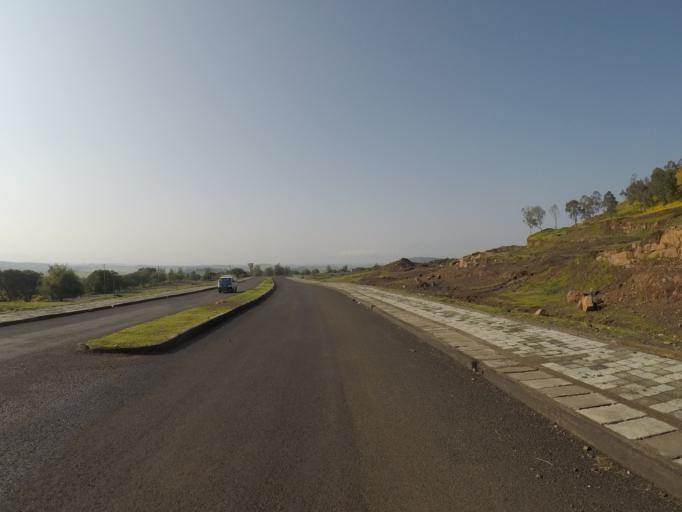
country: ET
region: Amhara
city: Gondar
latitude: 12.5287
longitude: 37.4303
